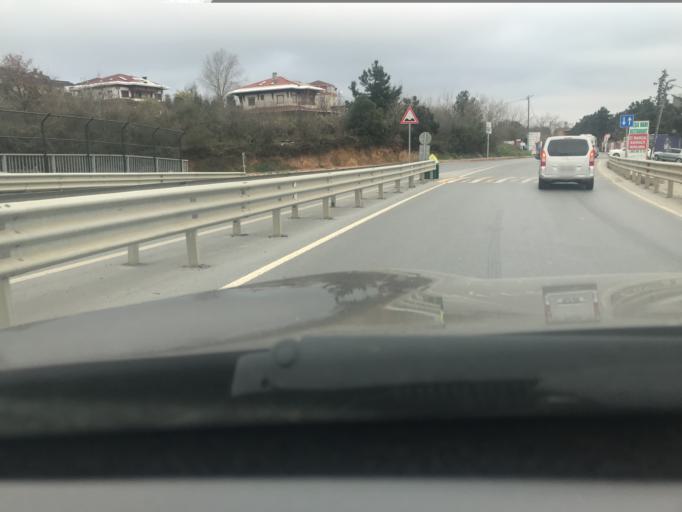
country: TR
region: Istanbul
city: Umraniye
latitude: 41.0530
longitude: 29.1708
